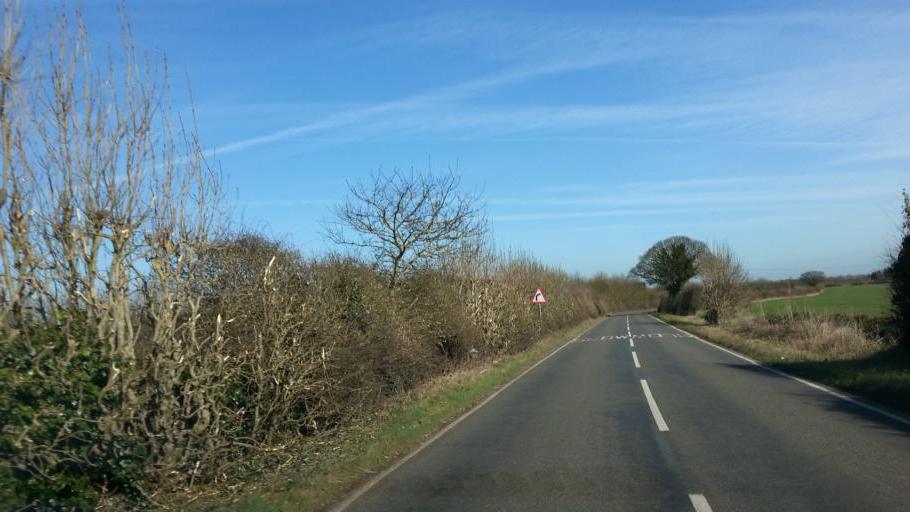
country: GB
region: England
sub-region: Northamptonshire
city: Desborough
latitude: 52.4047
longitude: -0.8481
